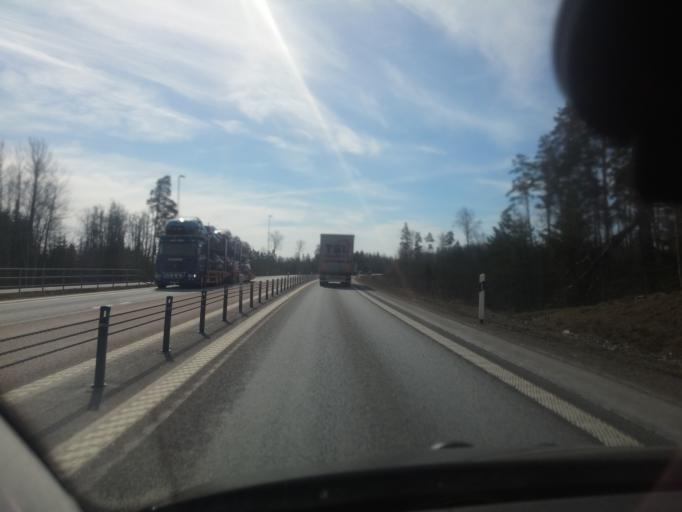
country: SE
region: Gaevleborg
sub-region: Gavle Kommun
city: Gavle
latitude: 60.7946
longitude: 17.0830
